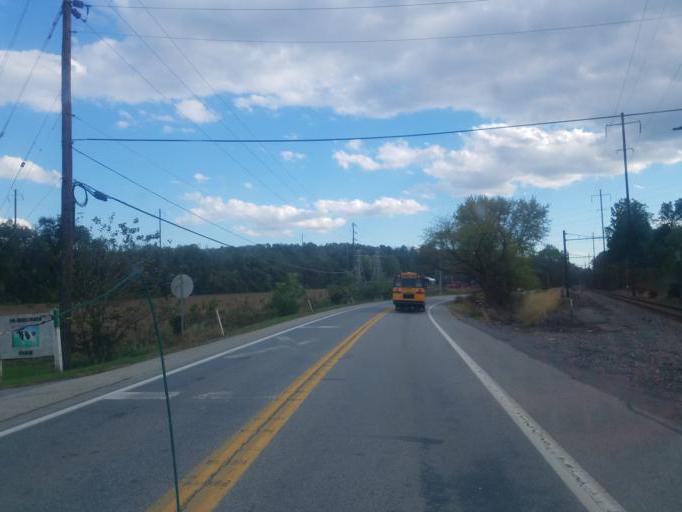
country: US
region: Pennsylvania
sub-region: Dauphin County
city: Middletown
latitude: 40.1825
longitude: -76.7258
